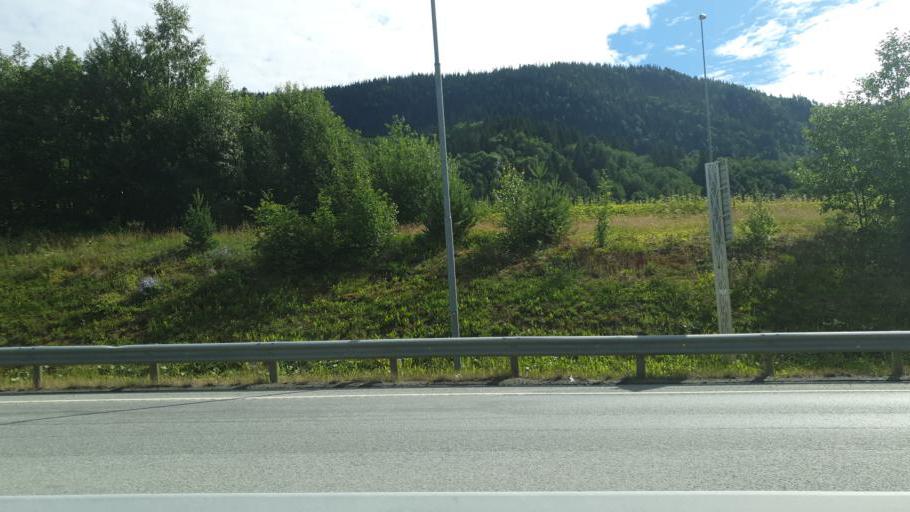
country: NO
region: Sor-Trondelag
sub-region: Melhus
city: Melhus
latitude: 63.2457
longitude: 10.2759
